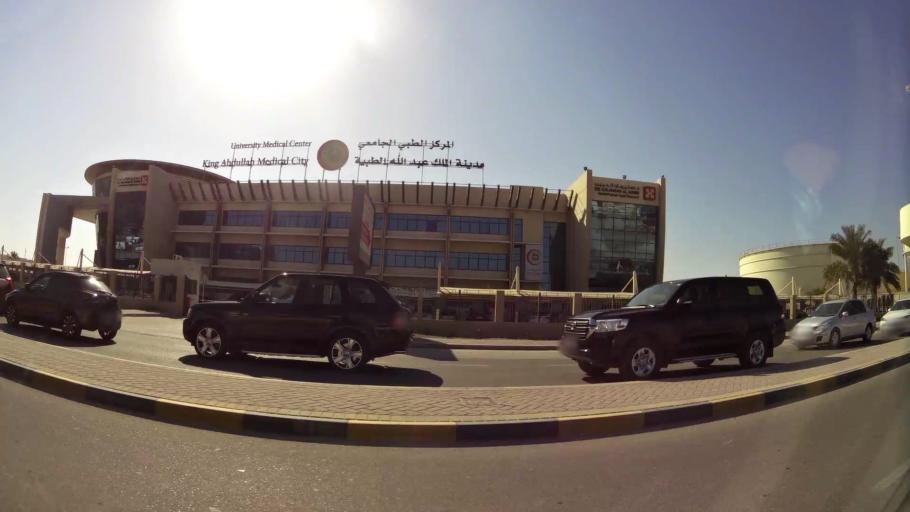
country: BH
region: Manama
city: Manama
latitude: 26.2135
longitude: 50.5756
